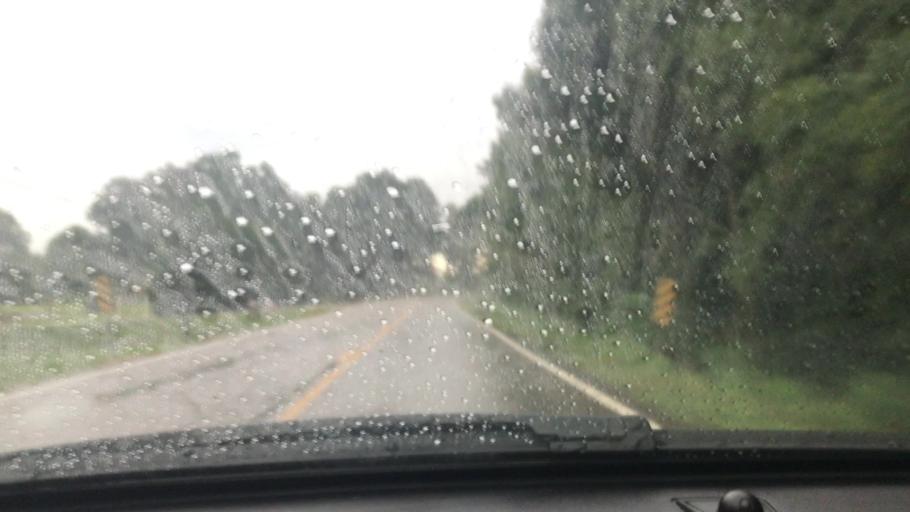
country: US
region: Mississippi
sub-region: Pike County
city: Summit
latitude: 31.3175
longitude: -90.5289
